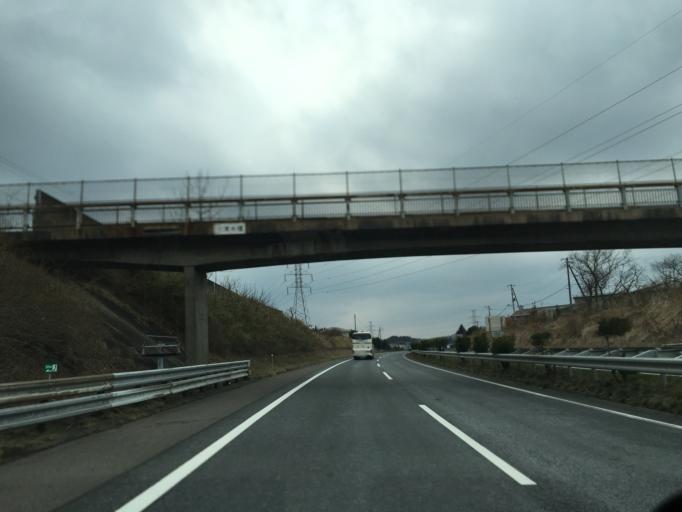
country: JP
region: Tochigi
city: Kuroiso
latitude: 37.1126
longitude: 140.1529
